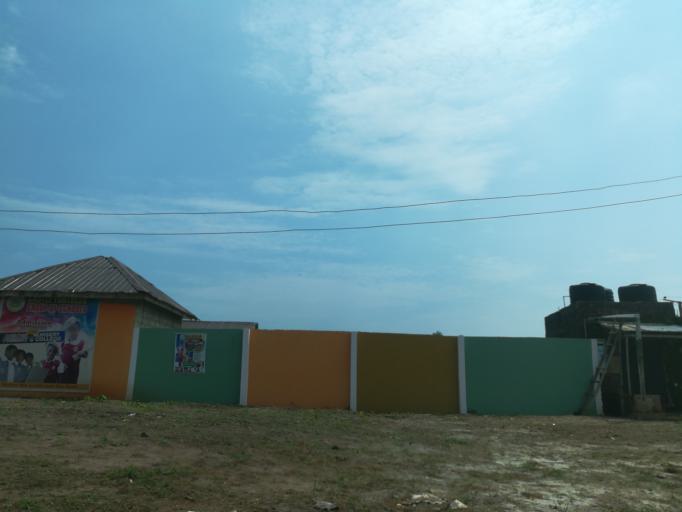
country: NG
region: Lagos
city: Ikorodu
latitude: 6.5924
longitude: 3.6421
